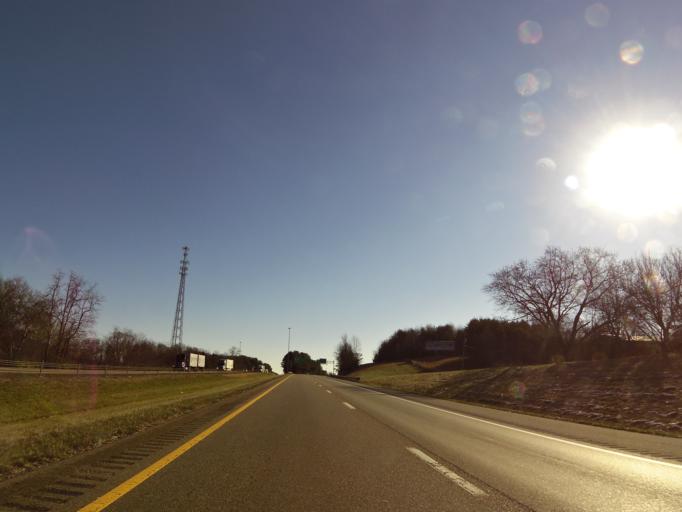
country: US
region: Tennessee
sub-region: Cocke County
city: Newport
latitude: 35.9721
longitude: -83.2646
